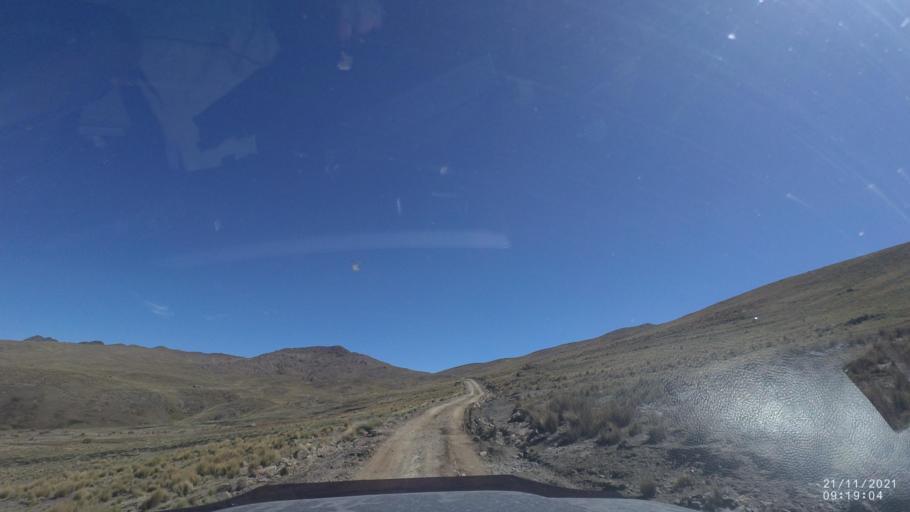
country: BO
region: Cochabamba
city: Cochabamba
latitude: -17.1162
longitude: -66.2543
